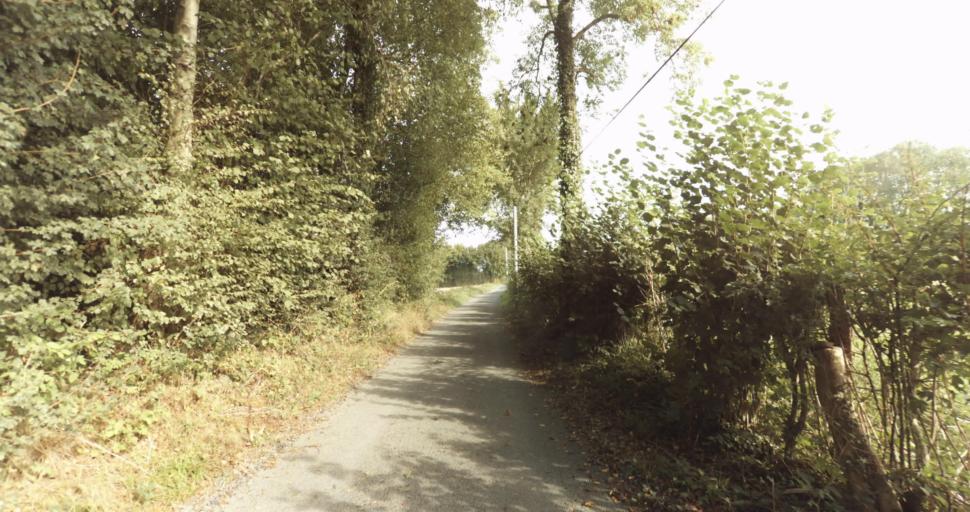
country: FR
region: Lower Normandy
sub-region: Departement de l'Orne
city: Gace
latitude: 48.8246
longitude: 0.2123
